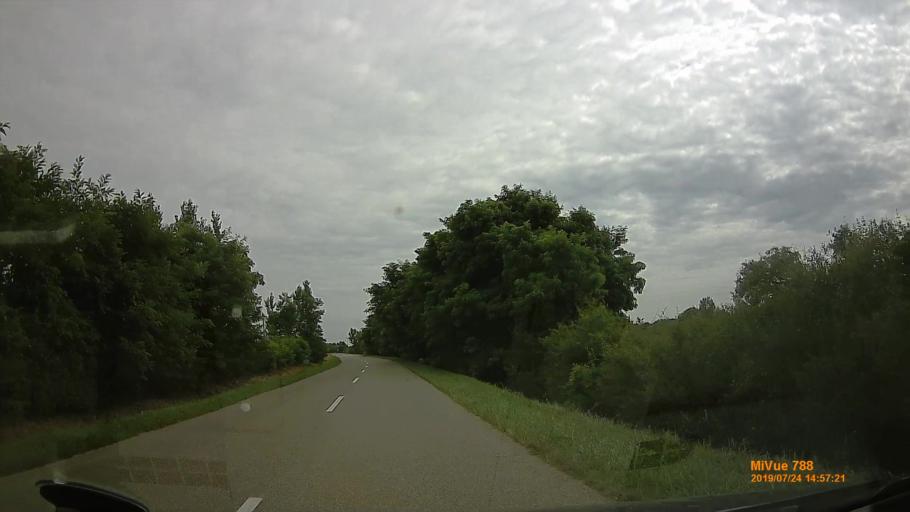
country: HU
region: Szabolcs-Szatmar-Bereg
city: Aranyosapati
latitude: 48.2337
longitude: 22.3199
